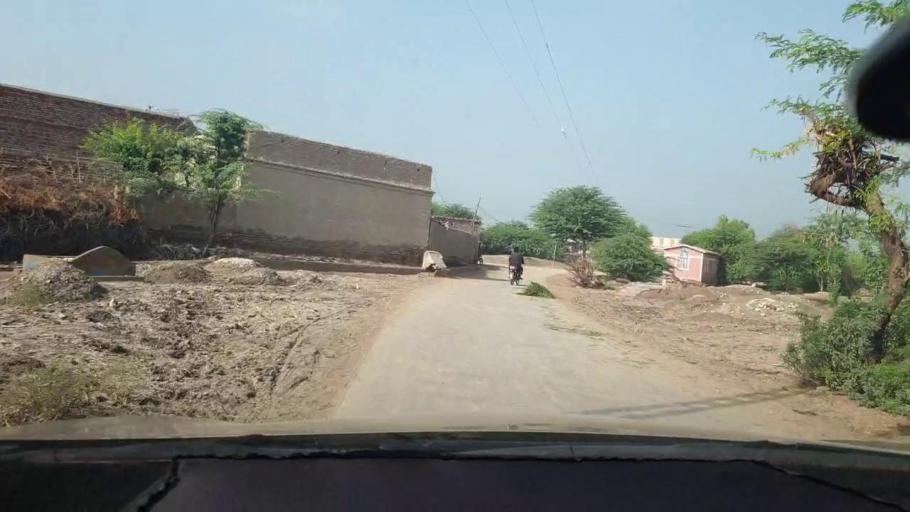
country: PK
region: Sindh
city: Goth Garelo
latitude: 27.4769
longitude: 68.0075
